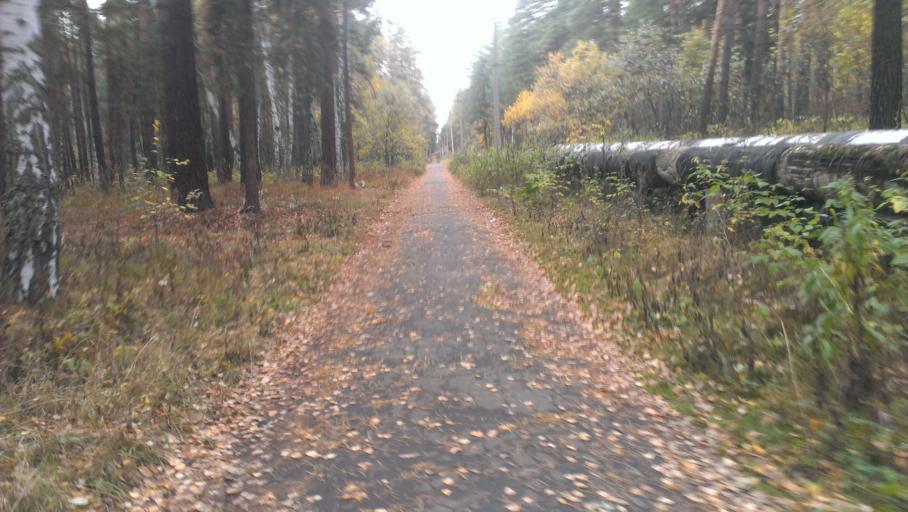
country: RU
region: Altai Krai
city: Yuzhnyy
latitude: 53.2615
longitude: 83.6876
